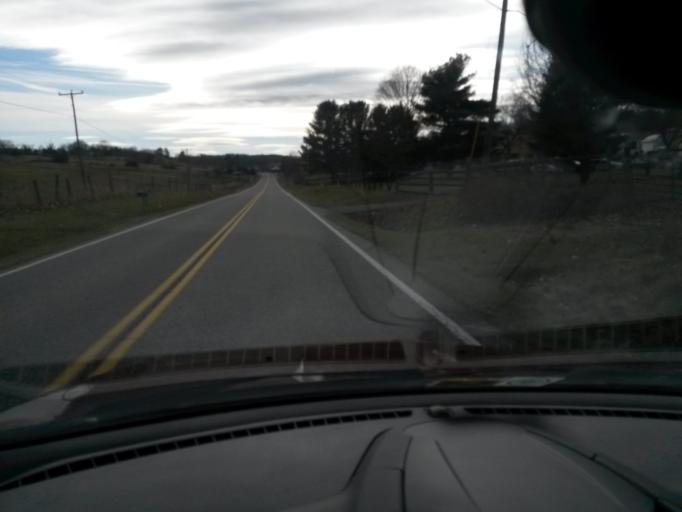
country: US
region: Virginia
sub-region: City of Staunton
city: Staunton
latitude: 38.2476
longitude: -79.1649
